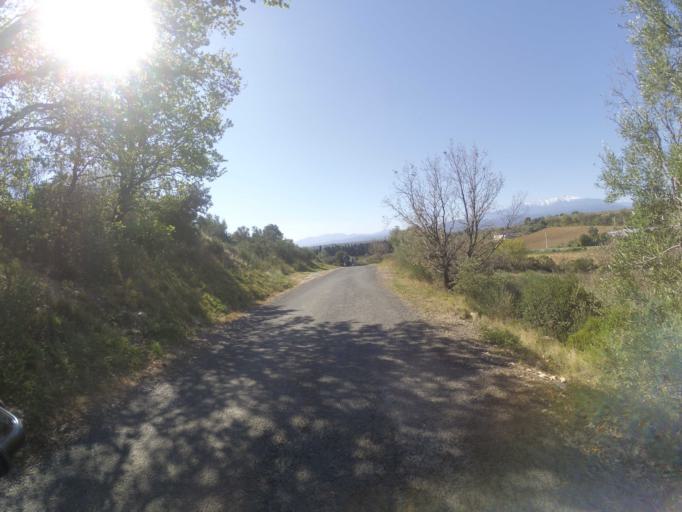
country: FR
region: Languedoc-Roussillon
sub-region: Departement des Pyrenees-Orientales
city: Pezilla-la-Riviere
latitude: 42.7076
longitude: 2.7754
